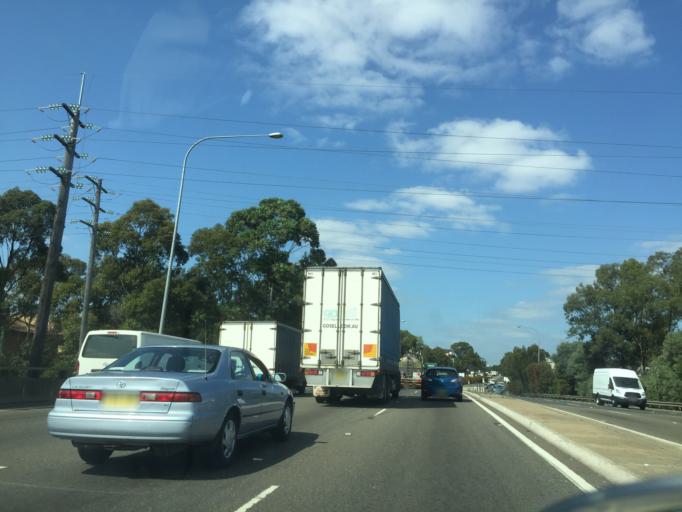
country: AU
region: New South Wales
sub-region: Strathfield
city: Homebush
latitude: -33.8641
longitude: 151.0663
